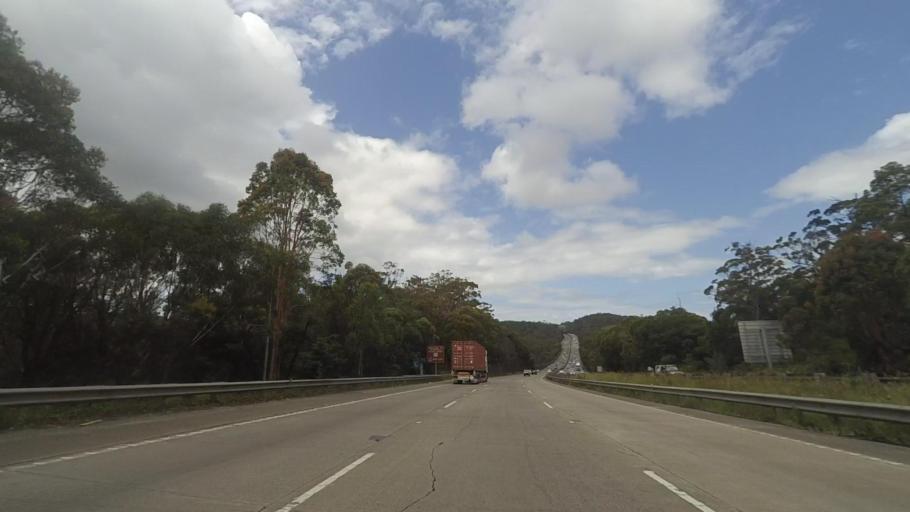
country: AU
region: New South Wales
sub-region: Gosford Shire
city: Point Clare
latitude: -33.4305
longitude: 151.2493
